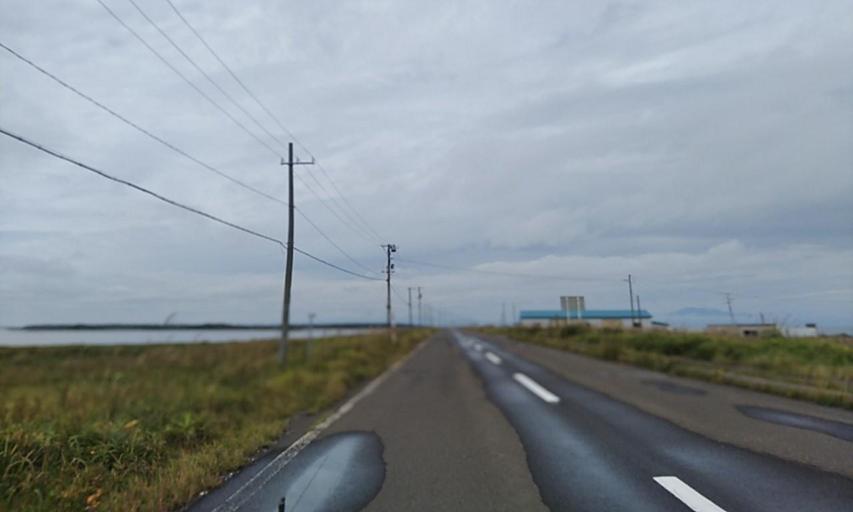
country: JP
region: Hokkaido
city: Shibetsu
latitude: 43.5979
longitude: 145.3184
